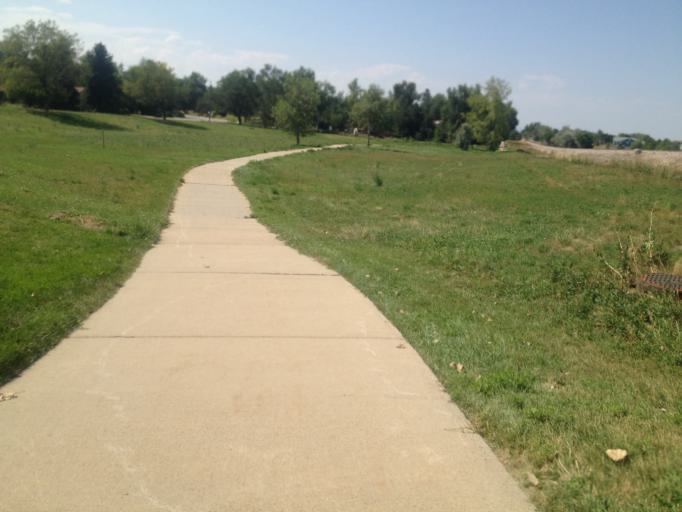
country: US
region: Colorado
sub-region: Boulder County
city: Louisville
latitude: 39.9906
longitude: -105.1347
